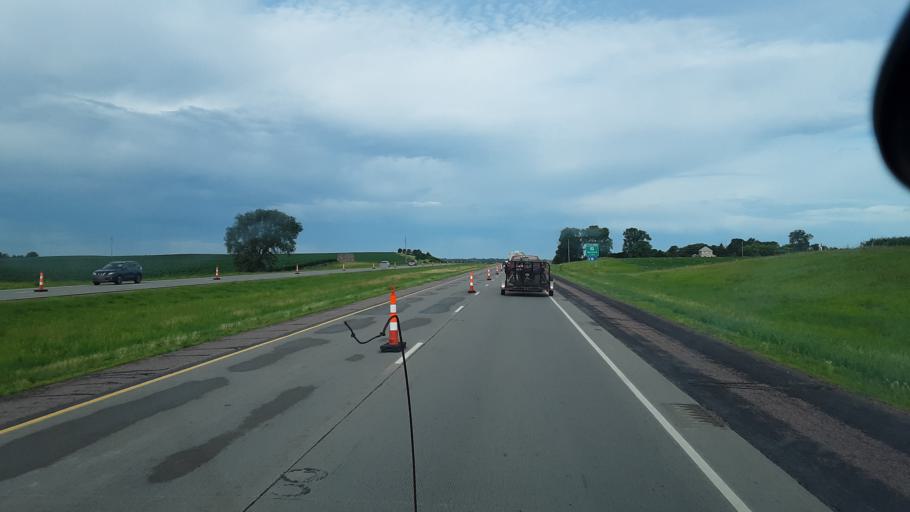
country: US
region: South Dakota
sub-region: Minnehaha County
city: Crooks
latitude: 43.6087
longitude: -96.8647
